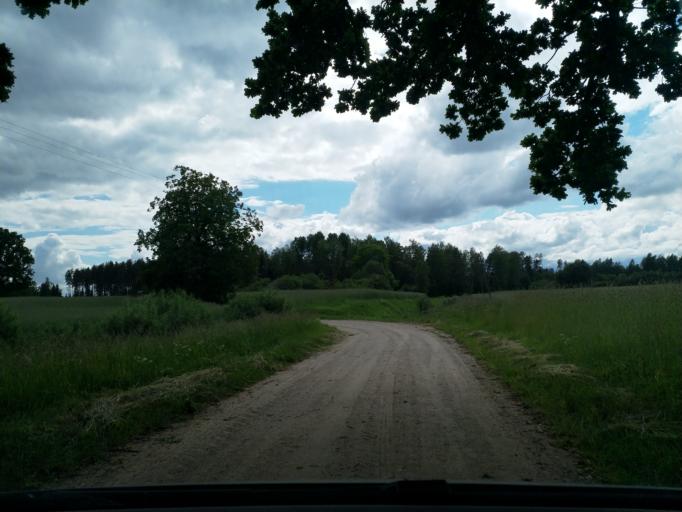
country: LV
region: Kuldigas Rajons
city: Kuldiga
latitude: 56.8354
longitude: 21.9552
